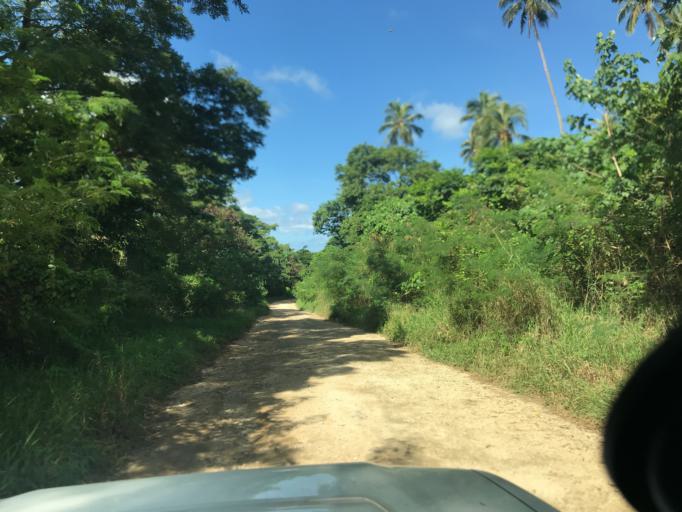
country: VU
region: Sanma
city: Luganville
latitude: -15.5229
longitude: 167.1480
